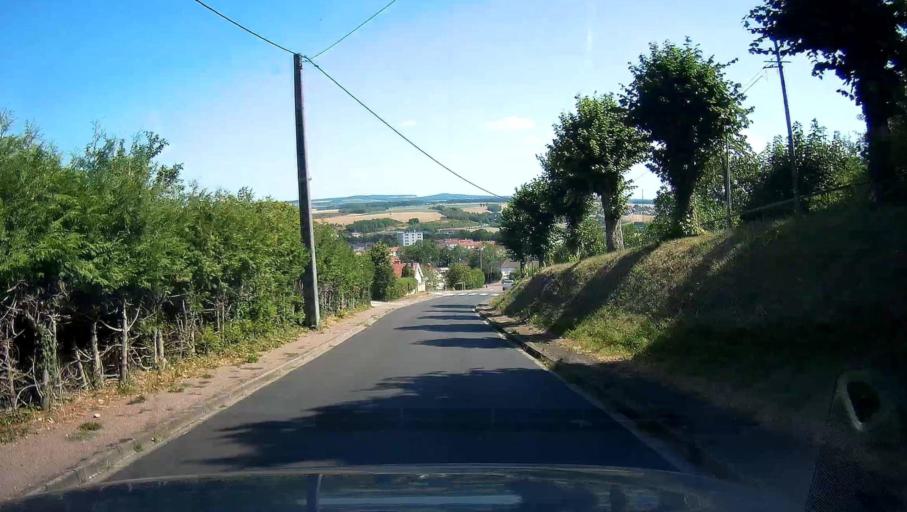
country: FR
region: Champagne-Ardenne
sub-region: Departement de la Haute-Marne
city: Langres
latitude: 47.8693
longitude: 5.3353
